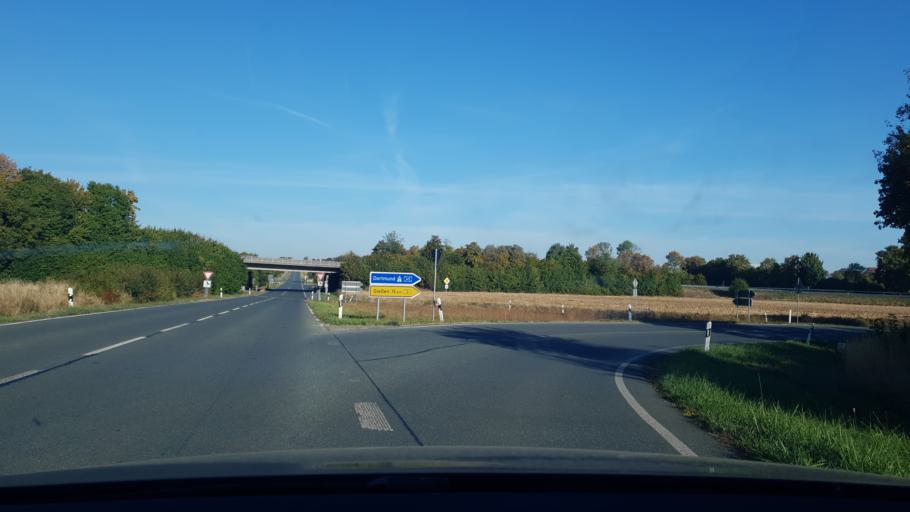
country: DE
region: Hesse
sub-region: Regierungsbezirk Darmstadt
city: Butzbach
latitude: 50.4638
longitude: 8.6431
